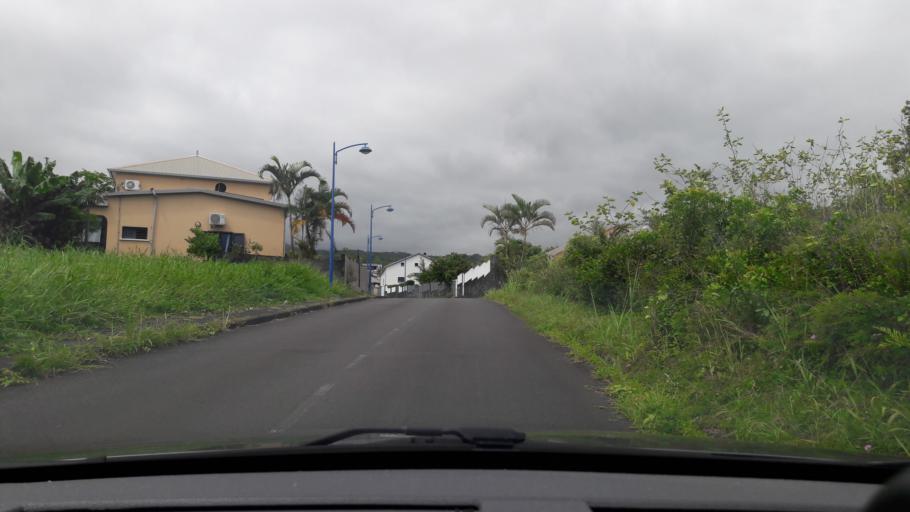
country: RE
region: Reunion
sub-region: Reunion
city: Saint-Benoit
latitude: -21.0928
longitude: 55.7040
